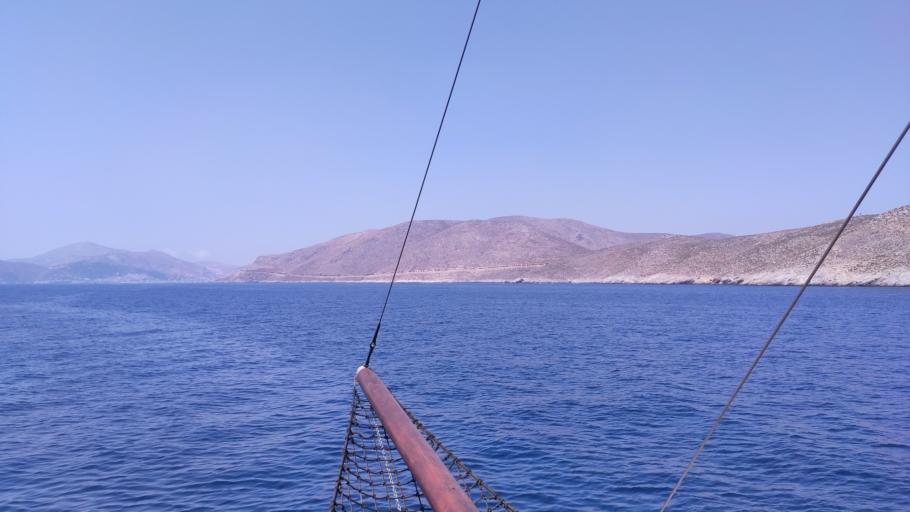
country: GR
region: South Aegean
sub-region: Nomos Dodekanisou
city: Kalymnos
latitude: 36.9403
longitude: 27.0519
